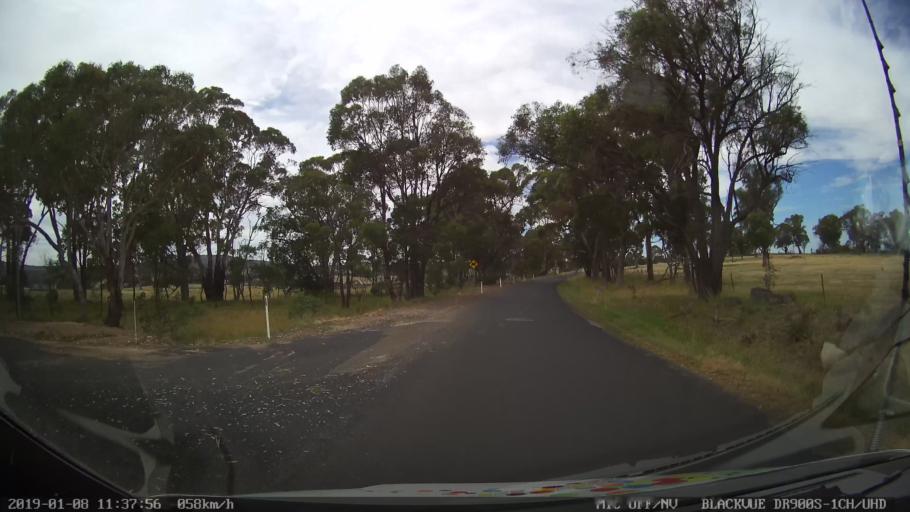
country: AU
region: New South Wales
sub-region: Guyra
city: Guyra
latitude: -30.3560
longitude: 151.5549
